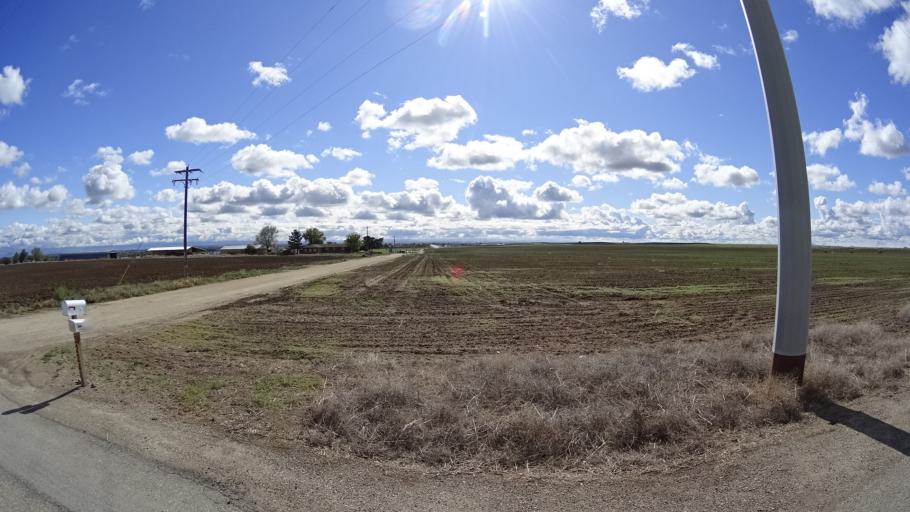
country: US
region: Idaho
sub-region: Ada County
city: Kuna
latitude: 43.4591
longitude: -116.4143
